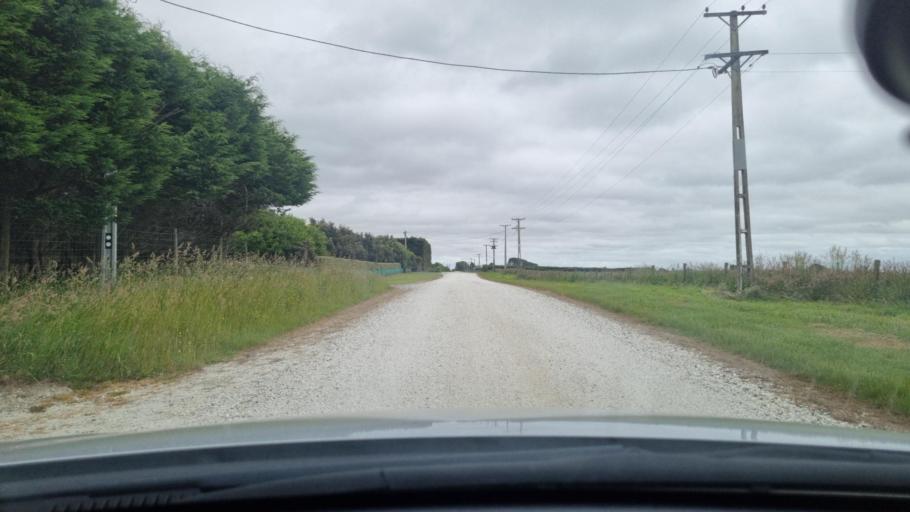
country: NZ
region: Southland
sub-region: Invercargill City
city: Invercargill
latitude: -46.3691
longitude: 168.3790
